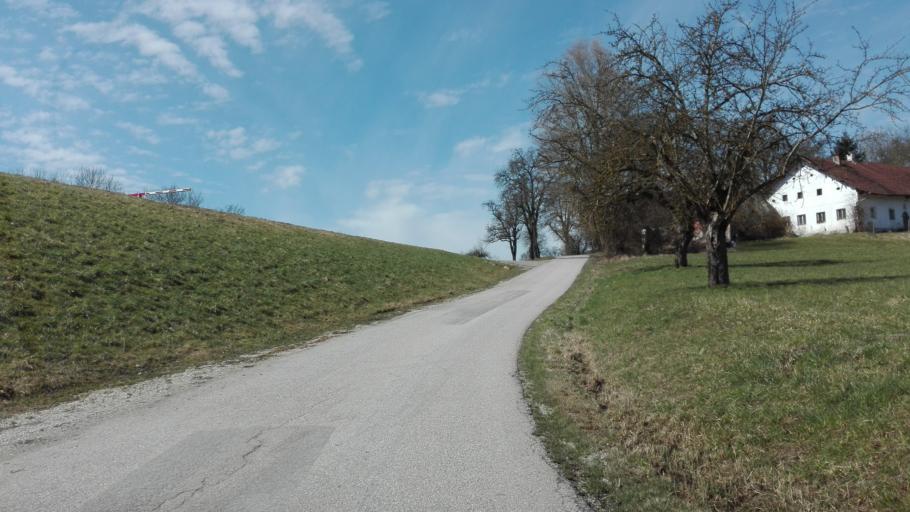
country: AT
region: Upper Austria
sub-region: Politischer Bezirk Grieskirchen
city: Bad Schallerbach
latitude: 48.2363
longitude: 13.8788
